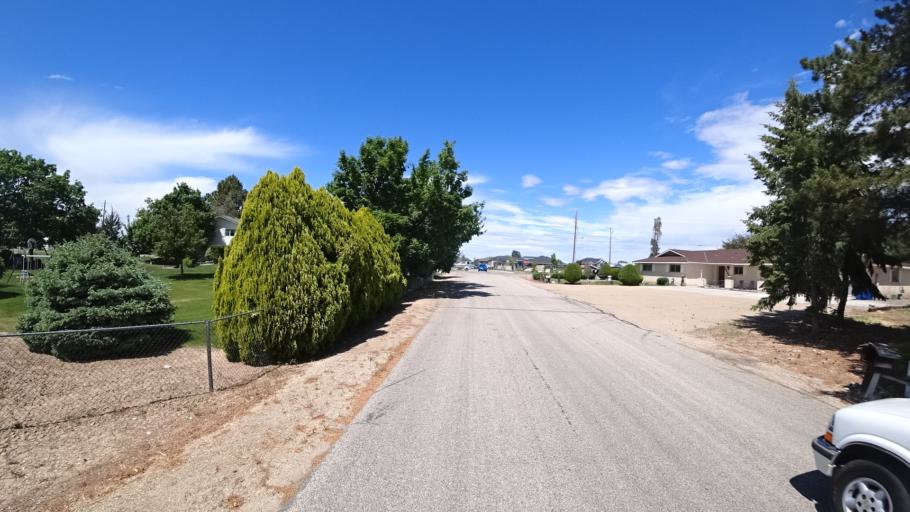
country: US
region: Idaho
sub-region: Ada County
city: Meridian
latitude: 43.5752
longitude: -116.3465
